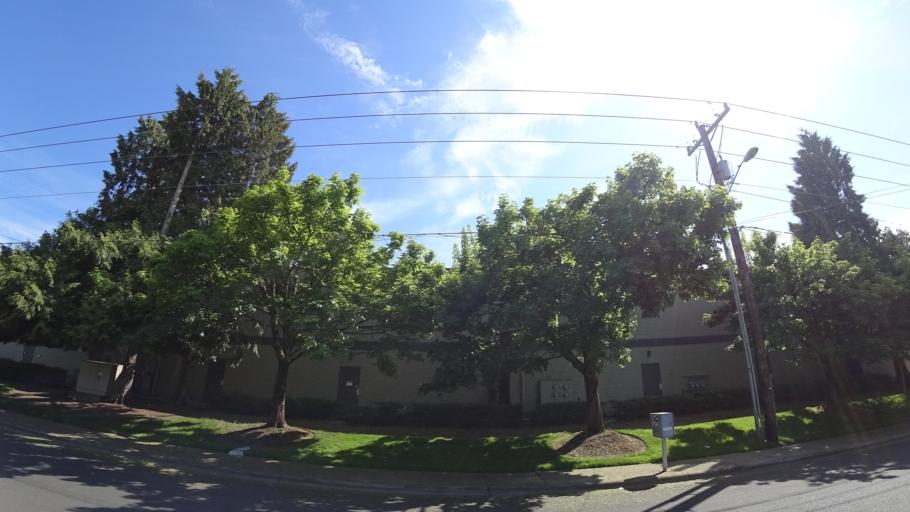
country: US
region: Oregon
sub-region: Washington County
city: Aloha
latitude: 45.4973
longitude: -122.8871
